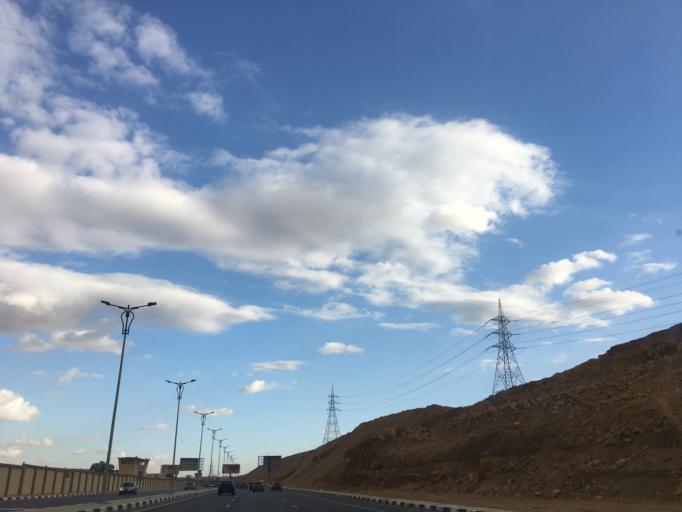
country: EG
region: Muhafazat al Qahirah
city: Cairo
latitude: 30.0209
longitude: 31.3302
